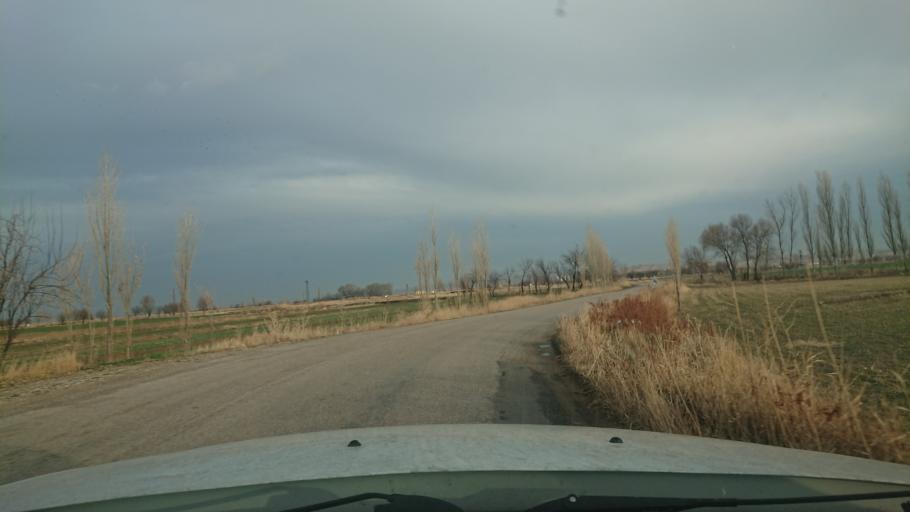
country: TR
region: Aksaray
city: Yesilova
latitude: 38.4416
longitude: 33.8367
